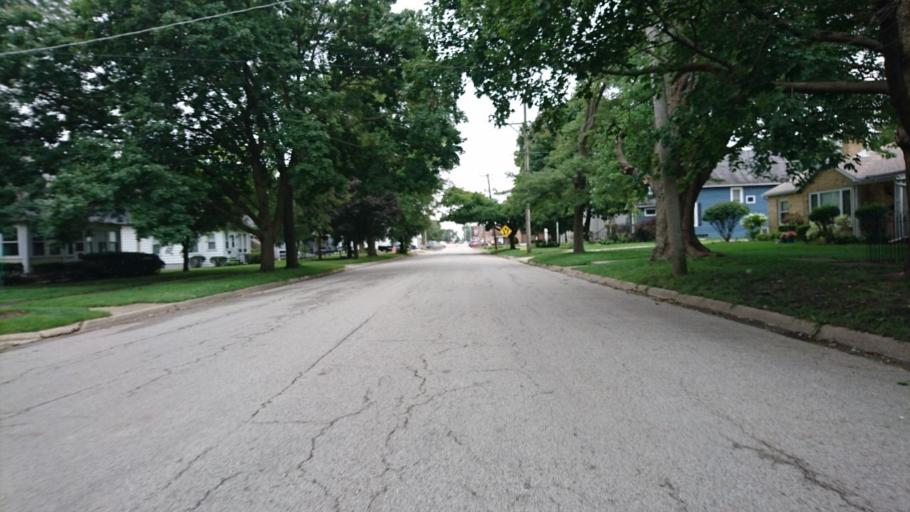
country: US
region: Illinois
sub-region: Livingston County
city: Dwight
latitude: 41.0962
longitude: -88.4262
